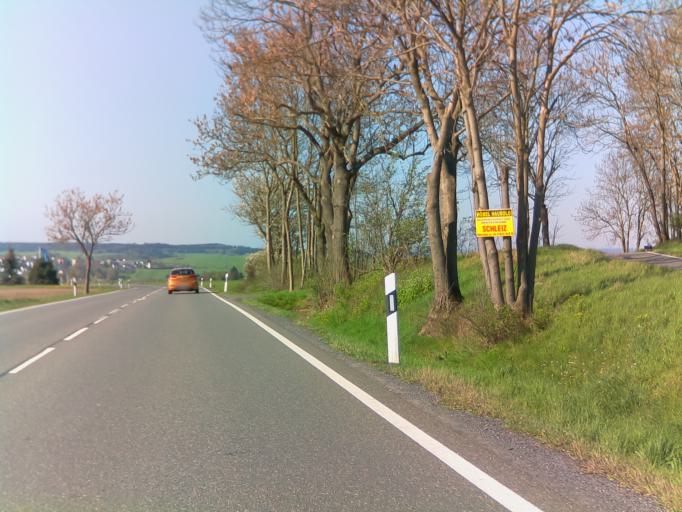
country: DE
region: Thuringia
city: Oettersdorf
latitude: 50.5913
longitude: 11.8142
